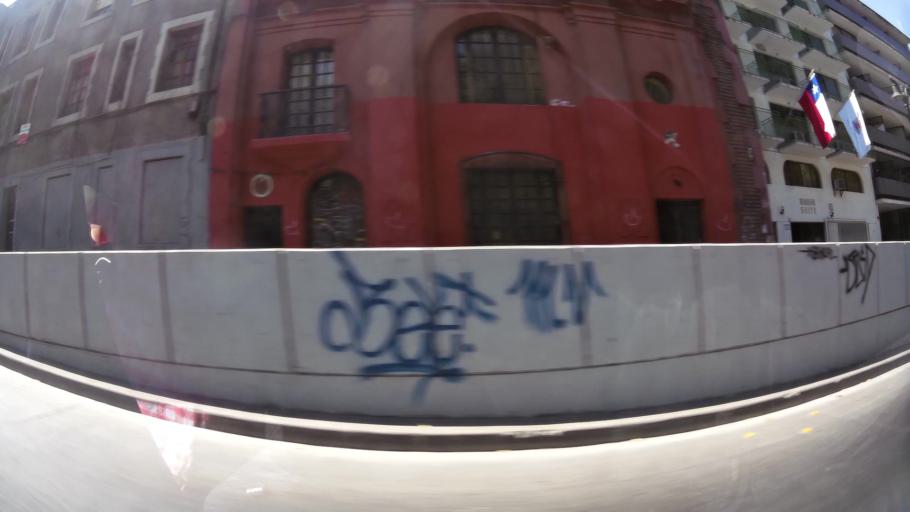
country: CL
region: Santiago Metropolitan
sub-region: Provincia de Santiago
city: Santiago
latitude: -33.4397
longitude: -70.6423
